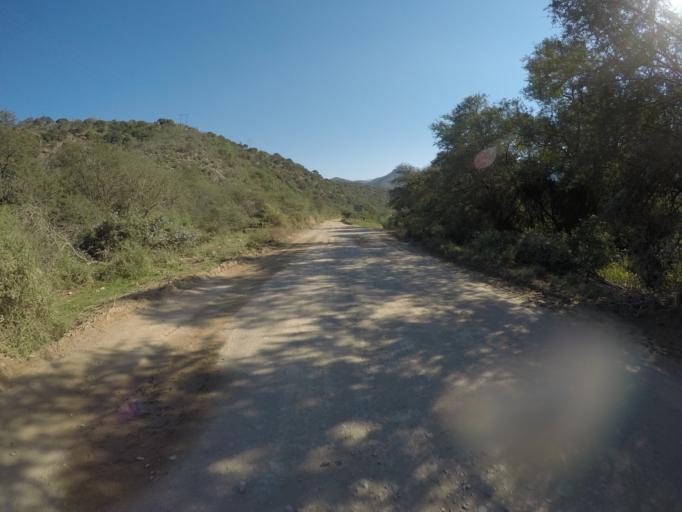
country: ZA
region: Eastern Cape
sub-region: Cacadu District Municipality
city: Kruisfontein
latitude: -33.6695
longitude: 24.5692
